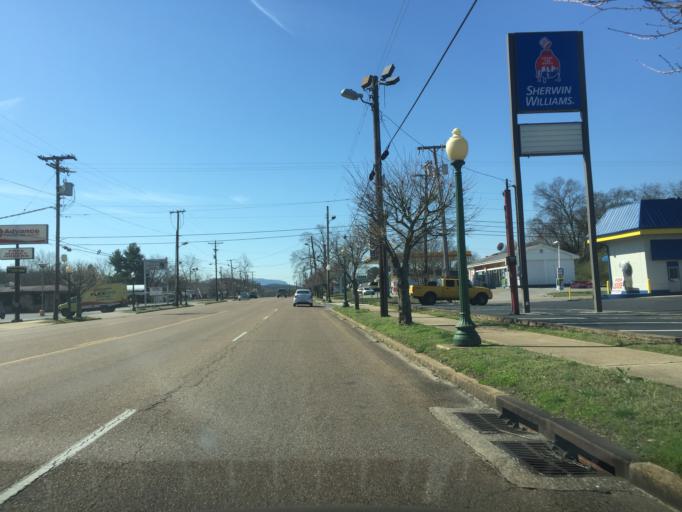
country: US
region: Tennessee
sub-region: Hamilton County
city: Red Bank
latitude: 35.1146
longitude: -85.2927
